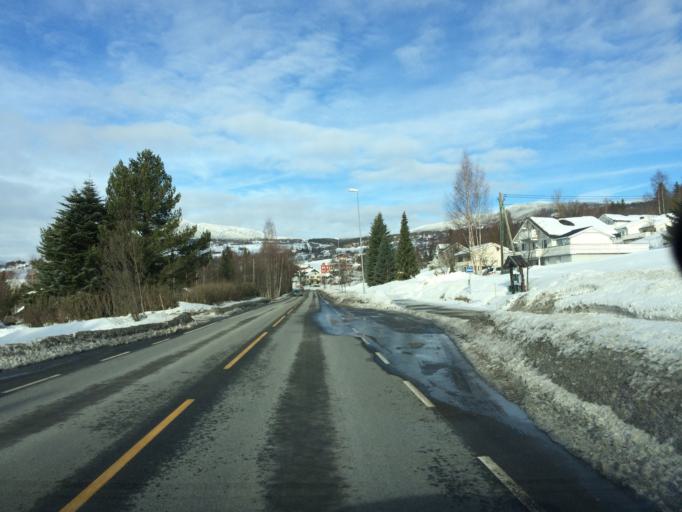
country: NO
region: Oppland
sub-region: Gausdal
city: Segalstad bru
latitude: 61.2112
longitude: 10.2949
